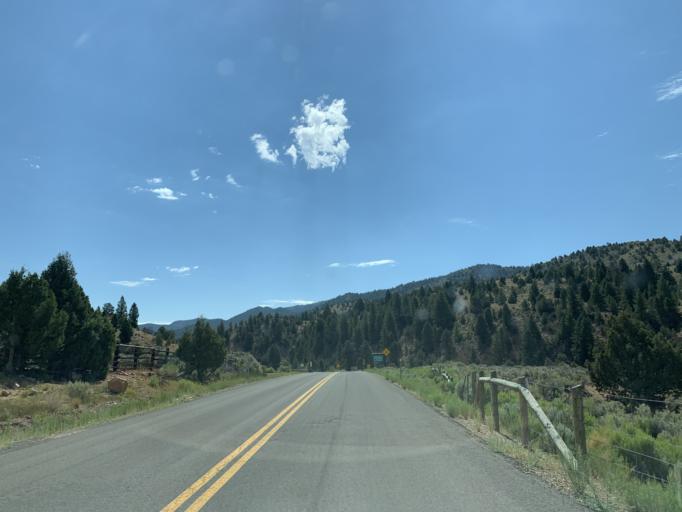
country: US
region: Utah
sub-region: Carbon County
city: East Carbon City
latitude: 39.7762
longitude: -110.4819
